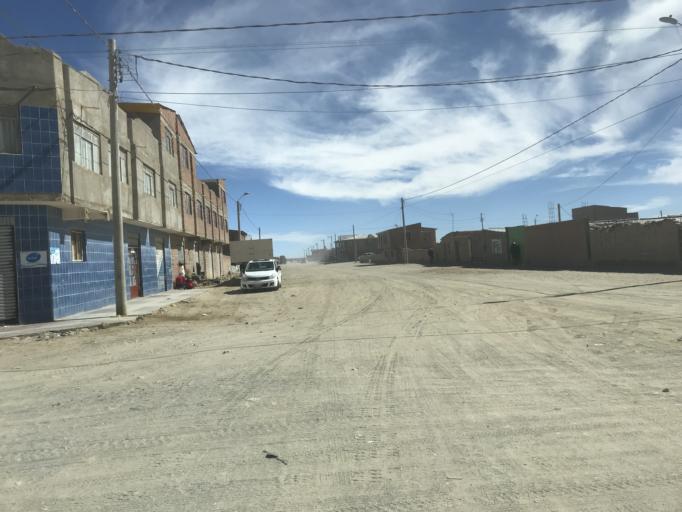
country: BO
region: Potosi
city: Uyuni
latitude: -20.4527
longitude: -66.8311
